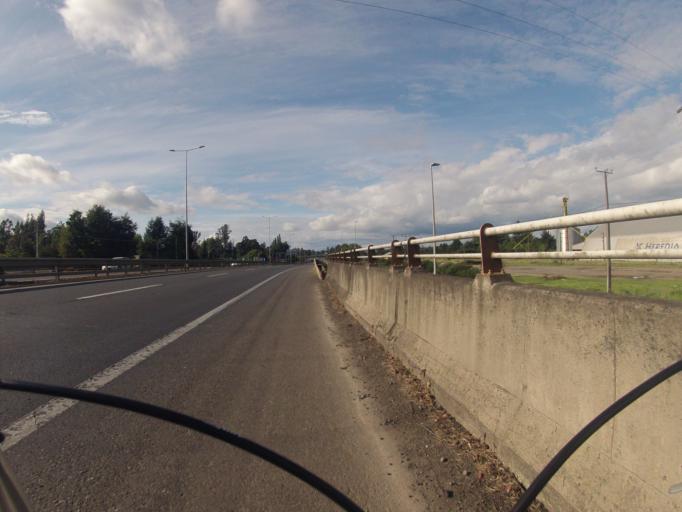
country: CL
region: Araucania
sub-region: Provincia de Cautin
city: Temuco
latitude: -38.8323
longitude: -72.6241
